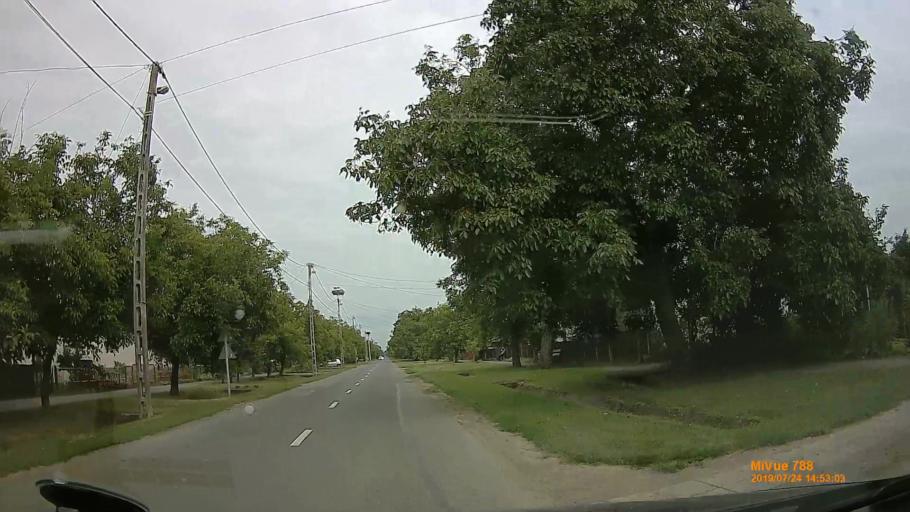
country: HU
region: Szabolcs-Szatmar-Bereg
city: Aranyosapati
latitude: 48.2587
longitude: 22.2899
